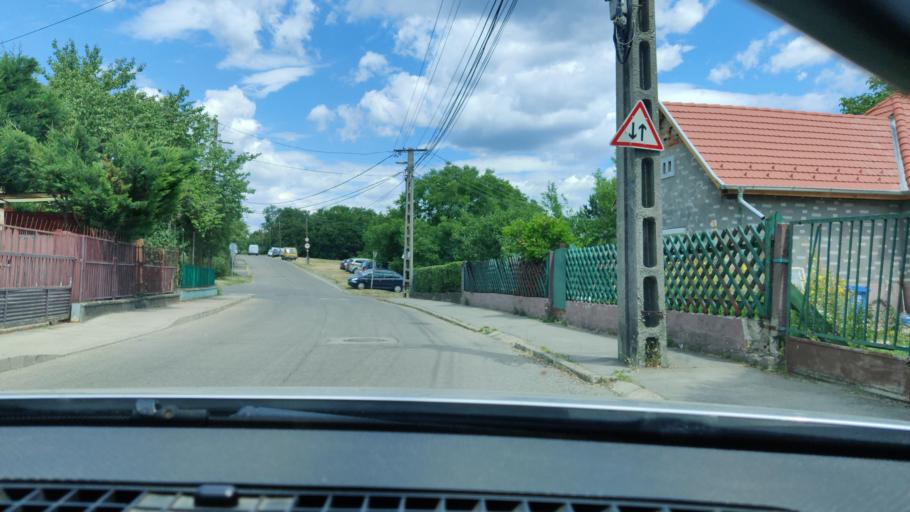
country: HU
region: Baranya
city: Pecs
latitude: 46.0863
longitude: 18.2623
